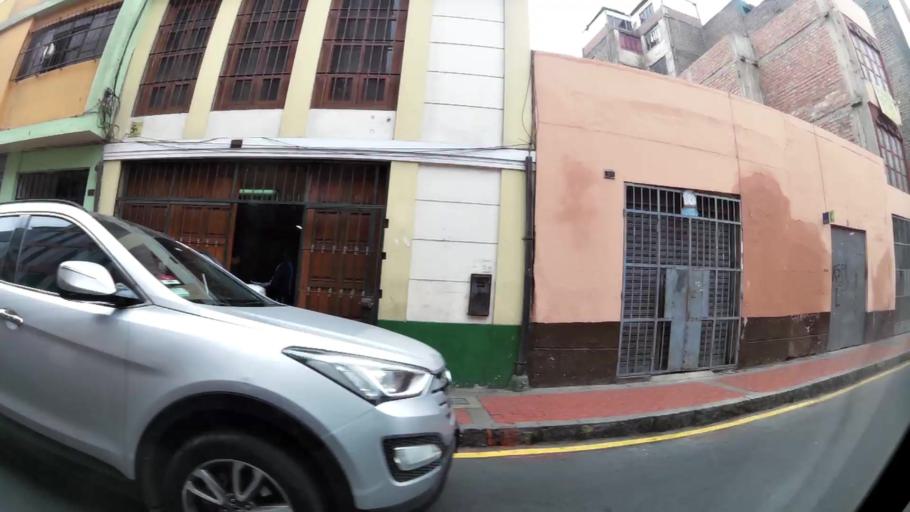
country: PE
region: Lima
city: Lima
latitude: -12.0448
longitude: -77.0348
